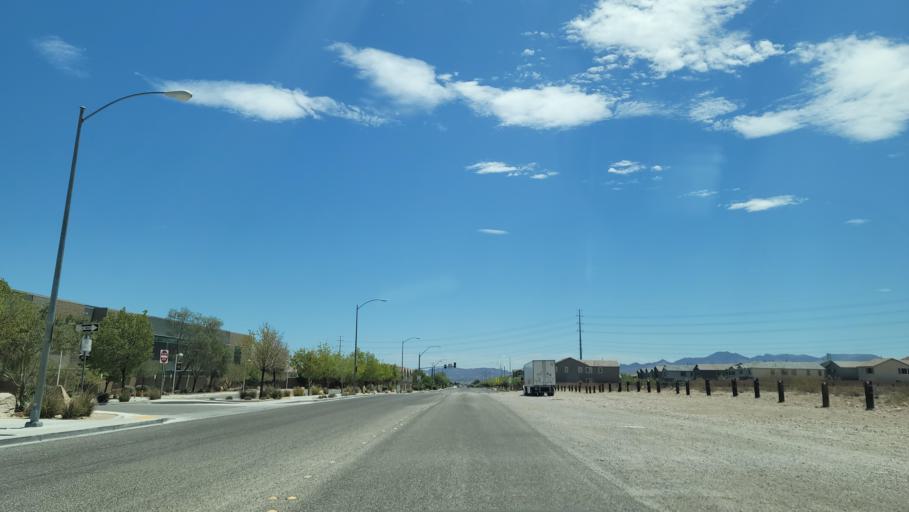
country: US
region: Nevada
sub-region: Clark County
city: Enterprise
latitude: 35.9914
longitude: -115.2378
